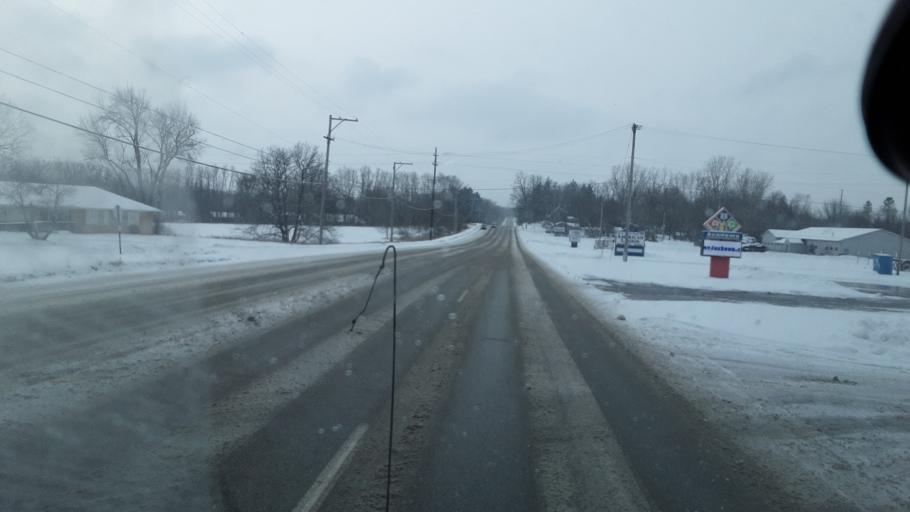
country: US
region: Michigan
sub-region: Jackson County
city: Jackson
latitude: 42.2901
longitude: -84.4137
